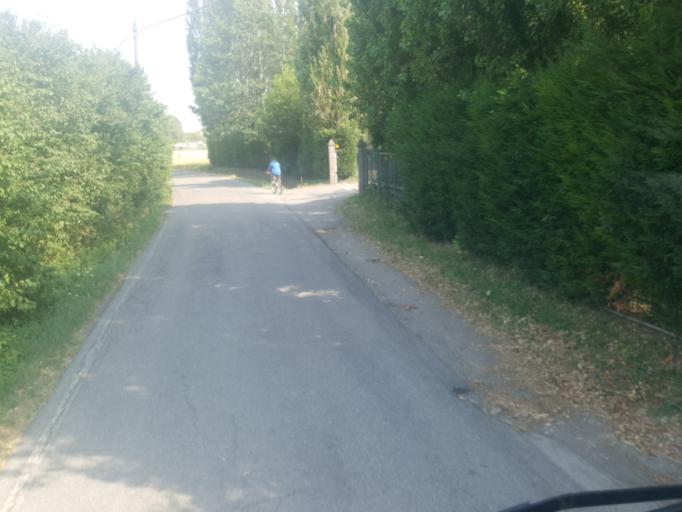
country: IT
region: Emilia-Romagna
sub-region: Provincia di Modena
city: Gaggio
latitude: 44.6372
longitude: 11.0064
